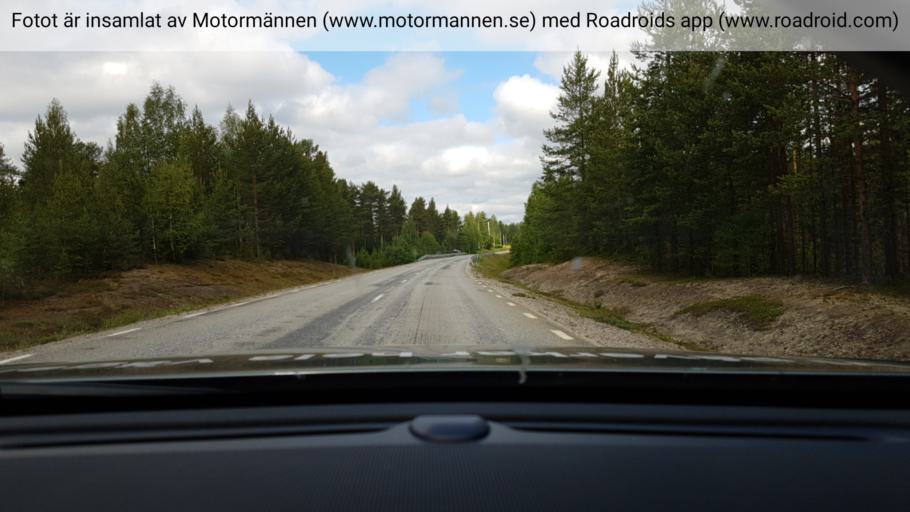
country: SE
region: Vaesterbotten
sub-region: Mala Kommun
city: Mala
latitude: 64.9038
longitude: 18.6900
